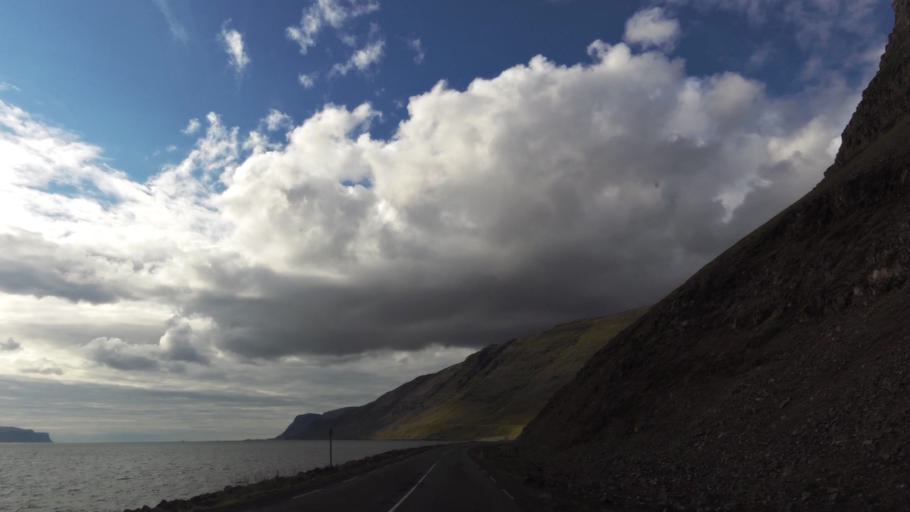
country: IS
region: West
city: Olafsvik
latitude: 65.5464
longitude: -23.8867
